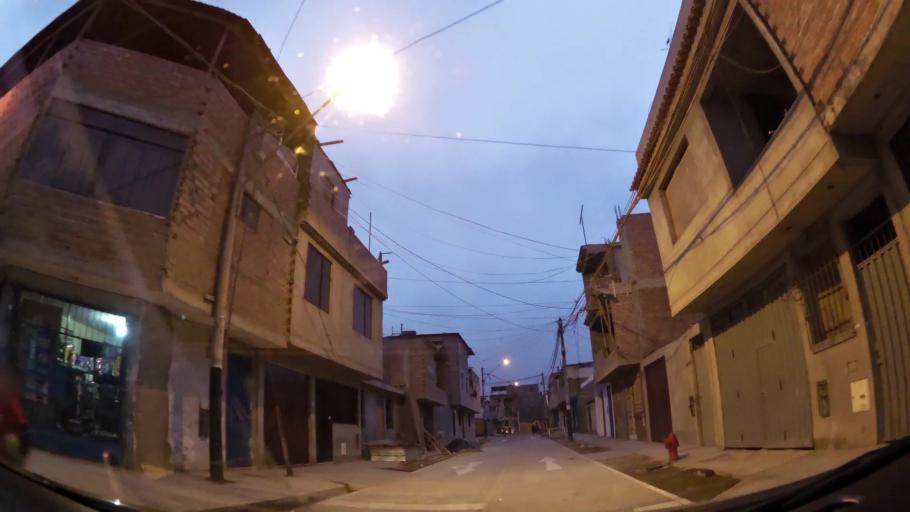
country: PE
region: Lima
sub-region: Lima
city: Surco
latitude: -12.1901
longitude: -76.9747
